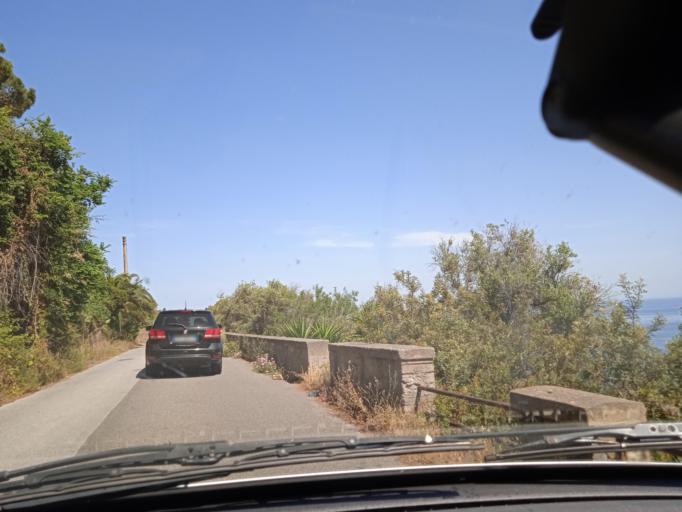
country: IT
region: Sicily
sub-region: Messina
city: Milazzo
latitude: 38.2572
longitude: 15.2467
